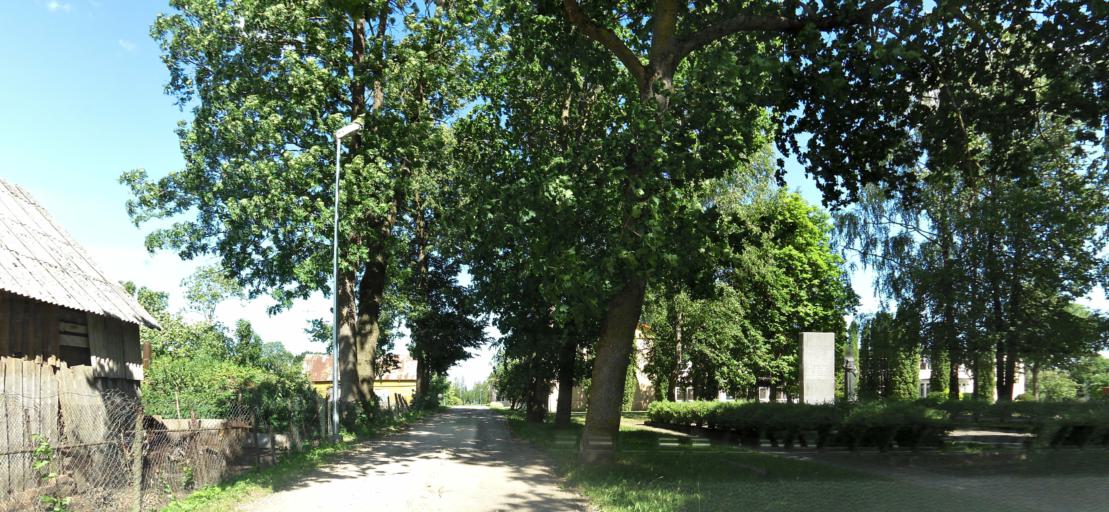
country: LT
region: Panevezys
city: Pasvalys
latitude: 56.1662
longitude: 24.2110
